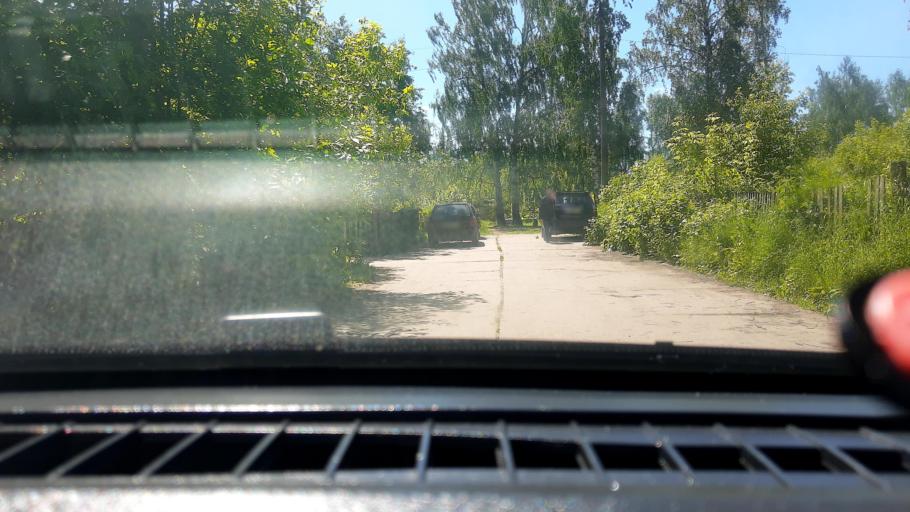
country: RU
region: Nizjnij Novgorod
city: Gorbatovka
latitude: 56.2159
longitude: 43.8027
